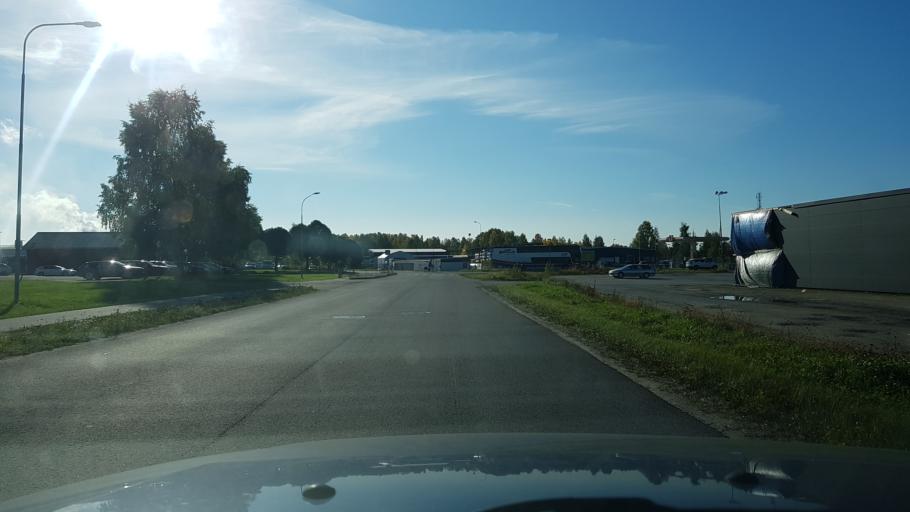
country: SE
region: Norrbotten
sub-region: Pitea Kommun
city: Bergsviken
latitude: 65.3417
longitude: 21.4095
